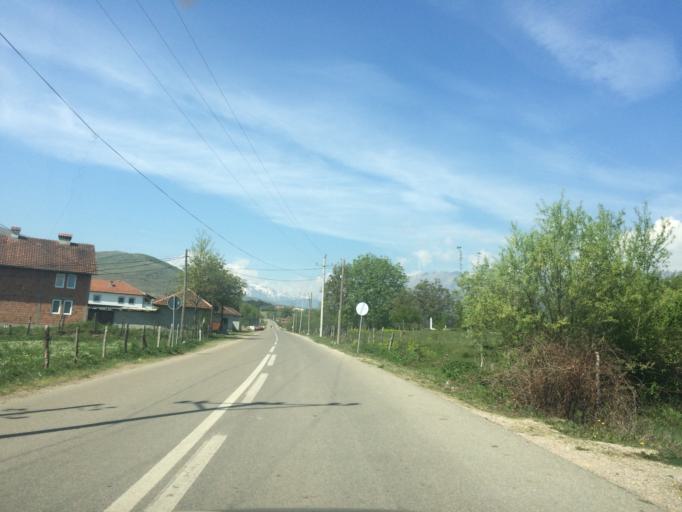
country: XK
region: Gjakova
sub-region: Komuna e Junikut
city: Junik
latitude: 42.4033
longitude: 20.2856
